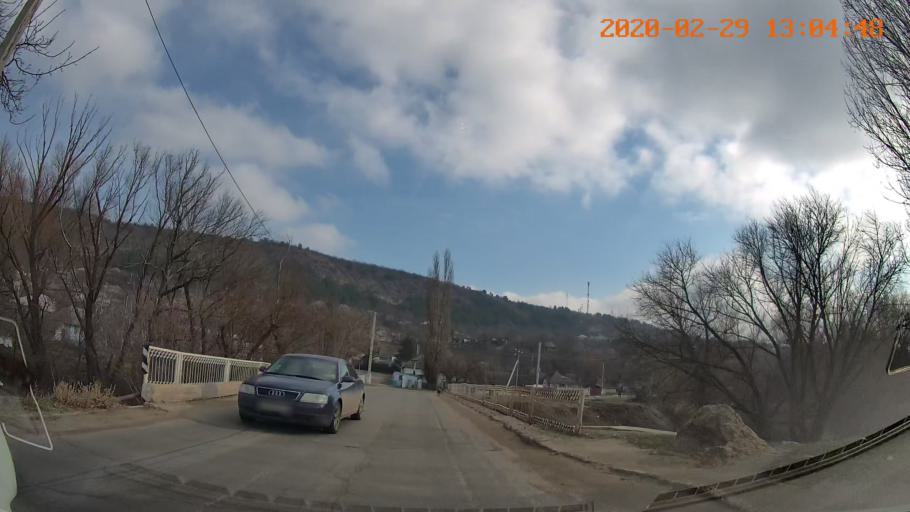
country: MD
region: Telenesti
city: Camenca
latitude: 48.0246
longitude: 28.7070
